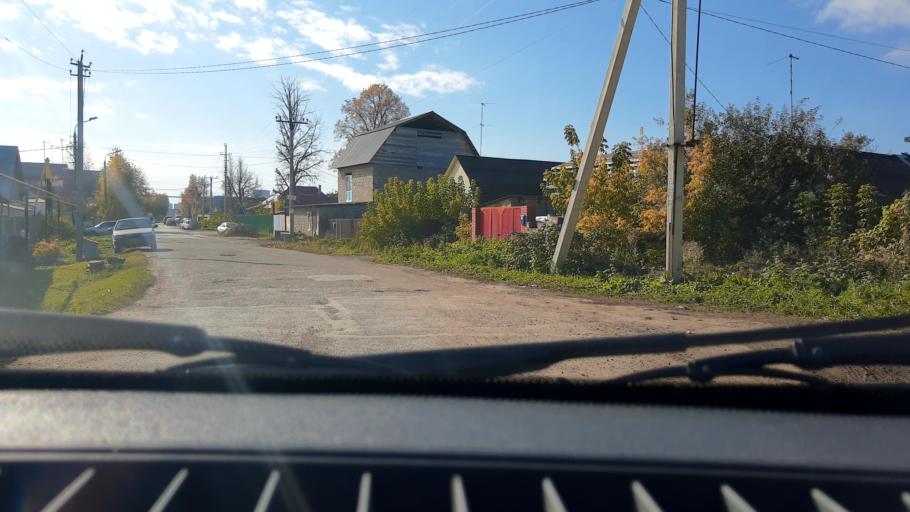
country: RU
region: Bashkortostan
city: Ufa
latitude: 54.7826
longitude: 56.0653
